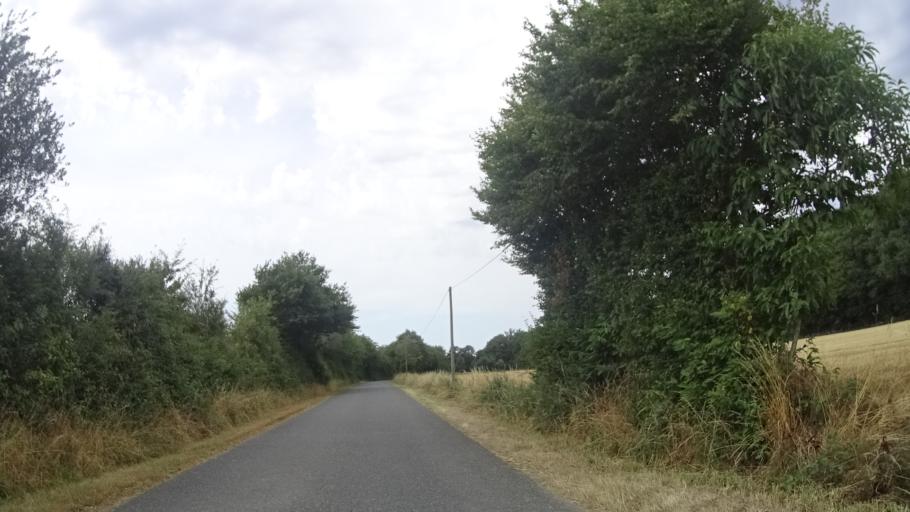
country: FR
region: Pays de la Loire
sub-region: Departement de la Loire-Atlantique
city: Fay-de-Bretagne
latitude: 47.4224
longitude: -1.7629
